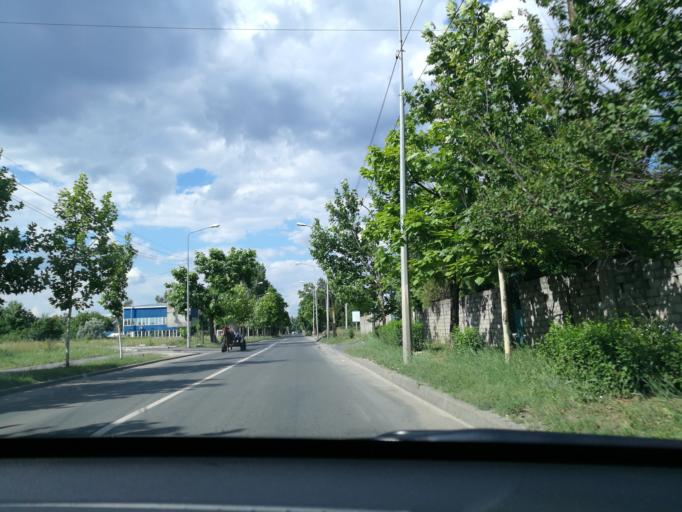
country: RO
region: Ilfov
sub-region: Comuna Glina
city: Catelu
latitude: 44.4176
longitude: 26.2180
